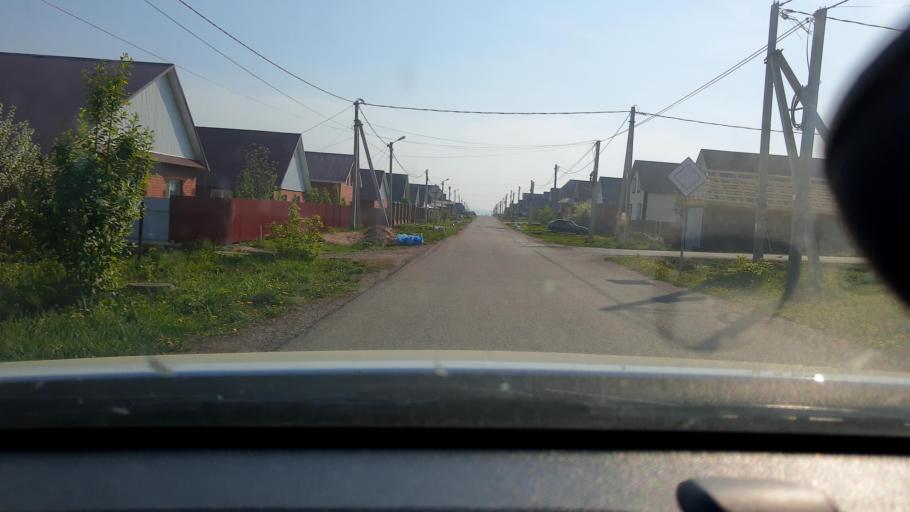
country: RU
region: Bashkortostan
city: Avdon
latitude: 54.6455
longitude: 55.7365
